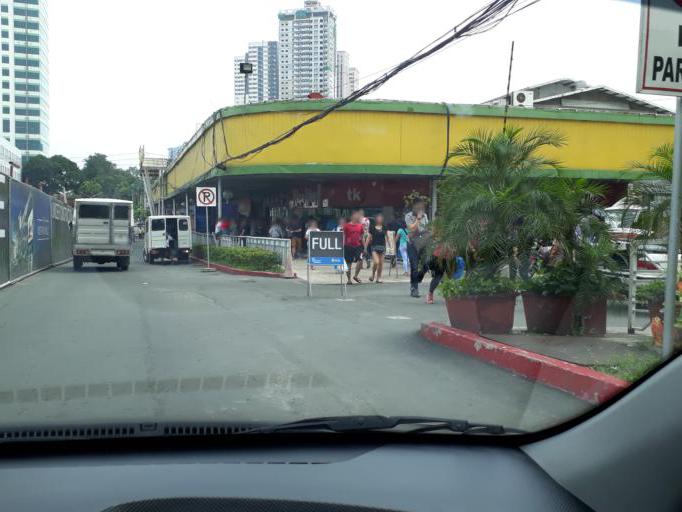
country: PH
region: Metro Manila
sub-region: San Juan
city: San Juan
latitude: 14.6204
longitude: 121.0526
